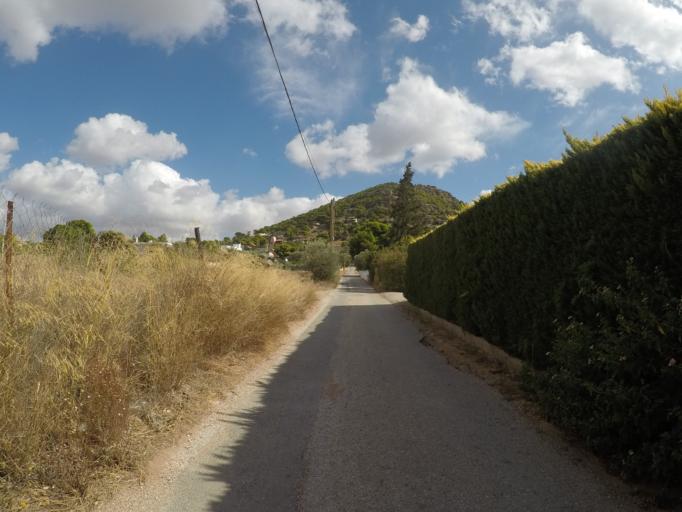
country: GR
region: Attica
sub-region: Nomarchia Anatolikis Attikis
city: Agia Marina
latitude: 37.8186
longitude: 23.8470
